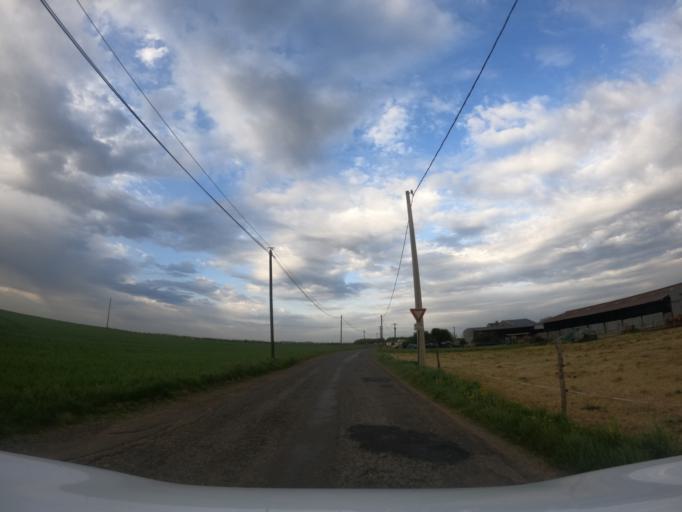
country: FR
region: Pays de la Loire
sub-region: Departement de la Vendee
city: Fontenay-le-Comte
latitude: 46.4334
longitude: -0.7948
